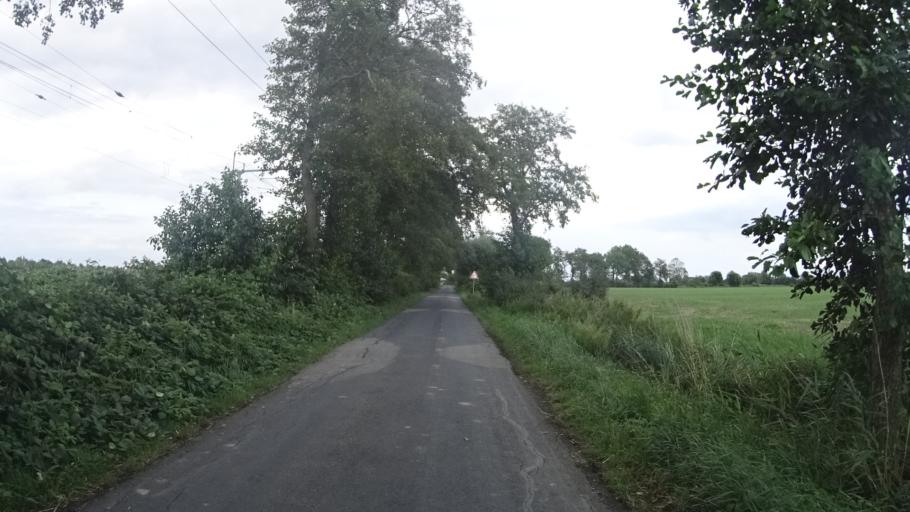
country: DE
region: Schleswig-Holstein
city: Herzhorn
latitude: 53.7813
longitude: 9.4669
